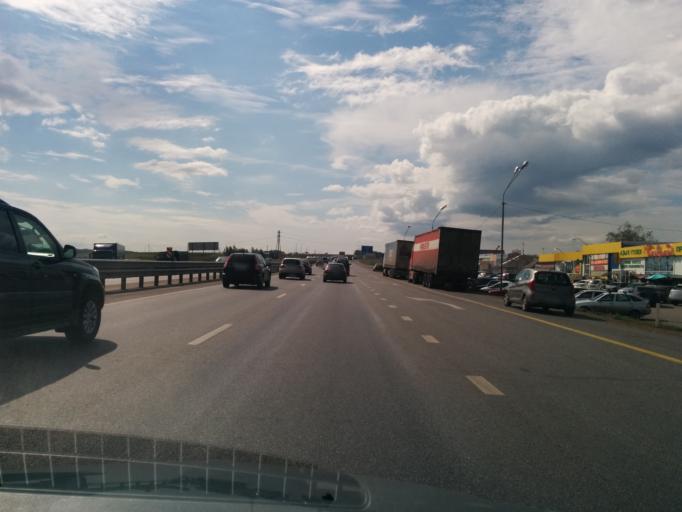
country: RU
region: Bashkortostan
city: Avdon
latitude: 54.4999
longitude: 55.9034
